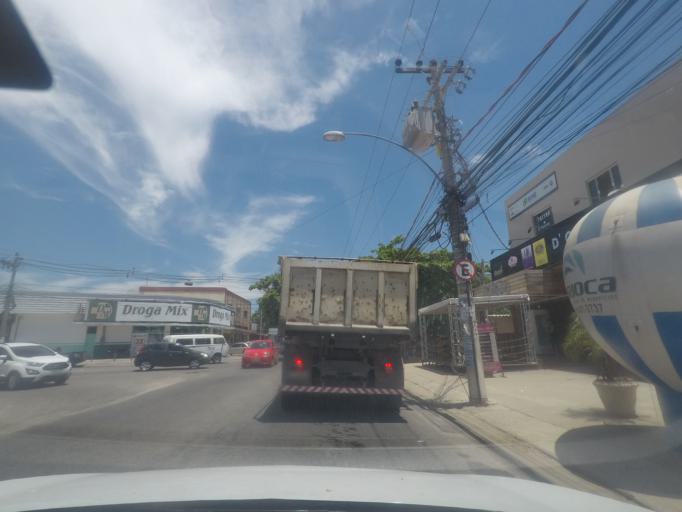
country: BR
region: Rio de Janeiro
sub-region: Itaguai
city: Itaguai
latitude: -22.9378
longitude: -43.6869
